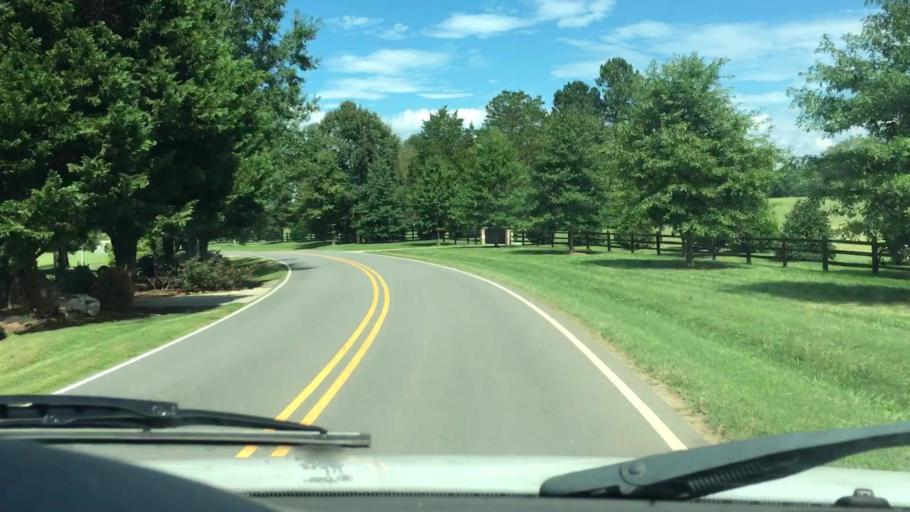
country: US
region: North Carolina
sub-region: Gaston County
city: Davidson
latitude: 35.4614
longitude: -80.8189
